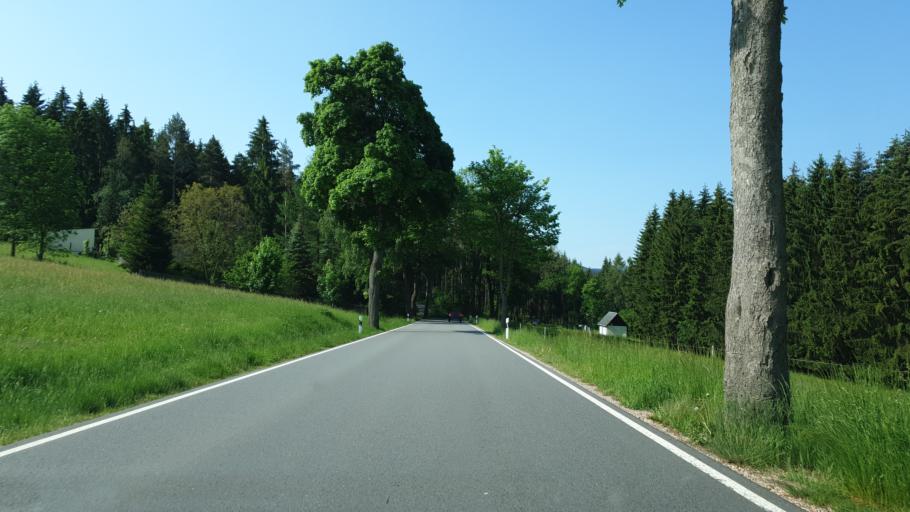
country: DE
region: Saxony
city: Eibenstock
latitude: 50.5284
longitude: 12.6206
